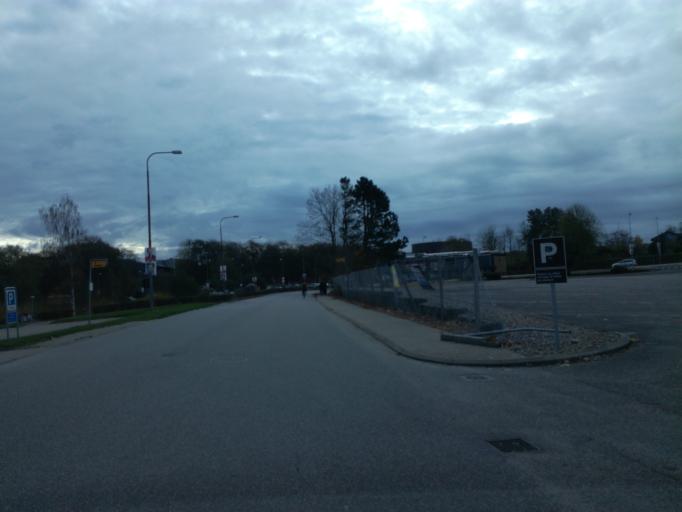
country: DK
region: South Denmark
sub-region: Fredericia Kommune
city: Fredericia
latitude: 55.5702
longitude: 9.7356
